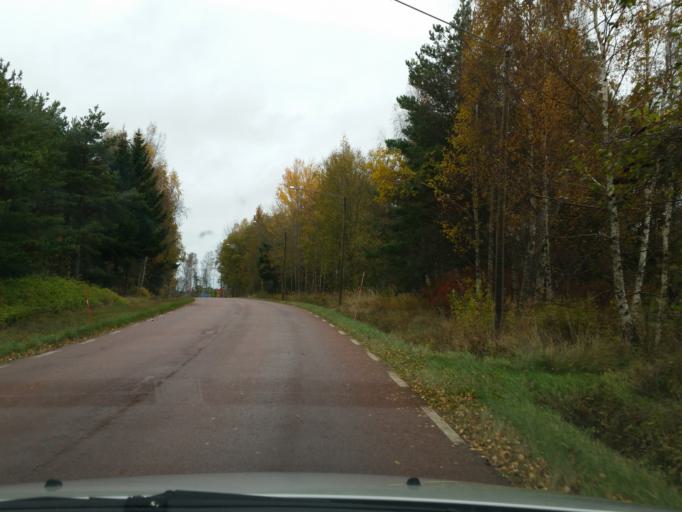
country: AX
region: Alands landsbygd
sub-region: Lemland
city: Lemland
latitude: 60.0669
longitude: 20.1014
